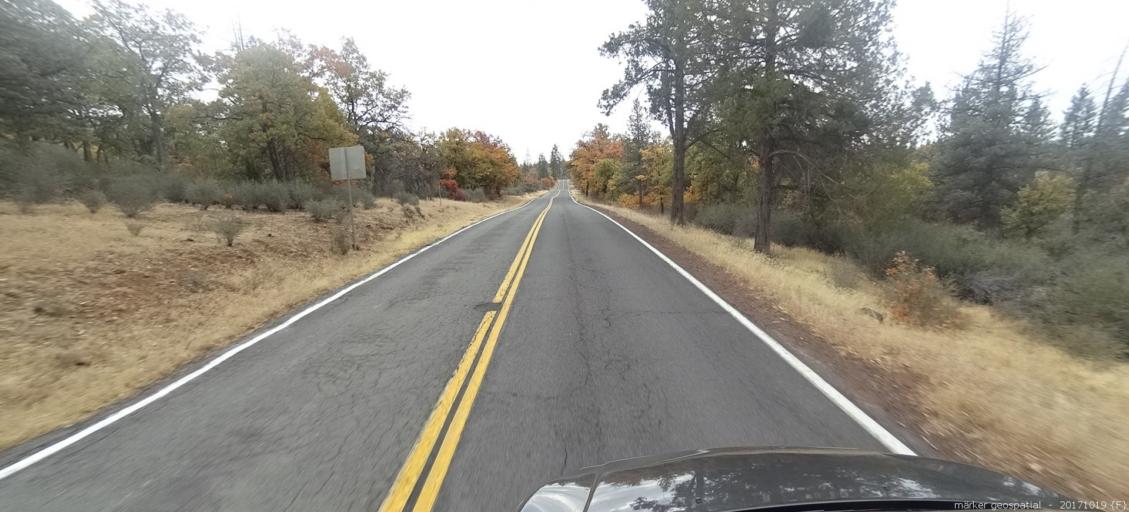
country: US
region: California
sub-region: Shasta County
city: Burney
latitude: 41.1500
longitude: -121.3528
